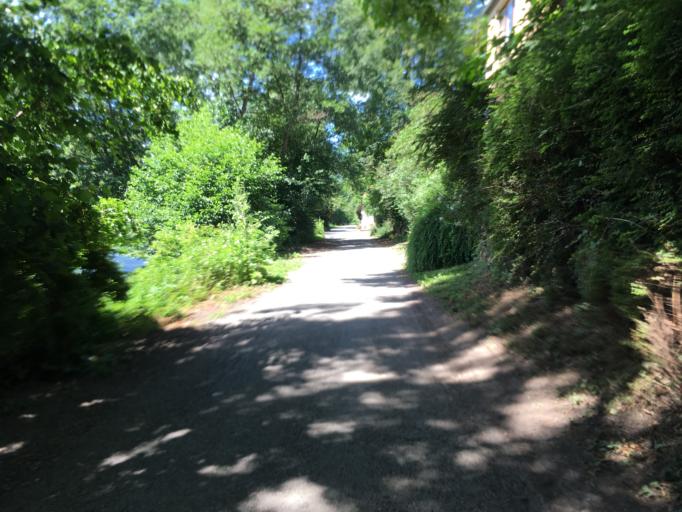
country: DE
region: Baden-Wuerttemberg
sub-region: Regierungsbezirk Stuttgart
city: Oberriexingen
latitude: 48.9242
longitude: 9.0206
